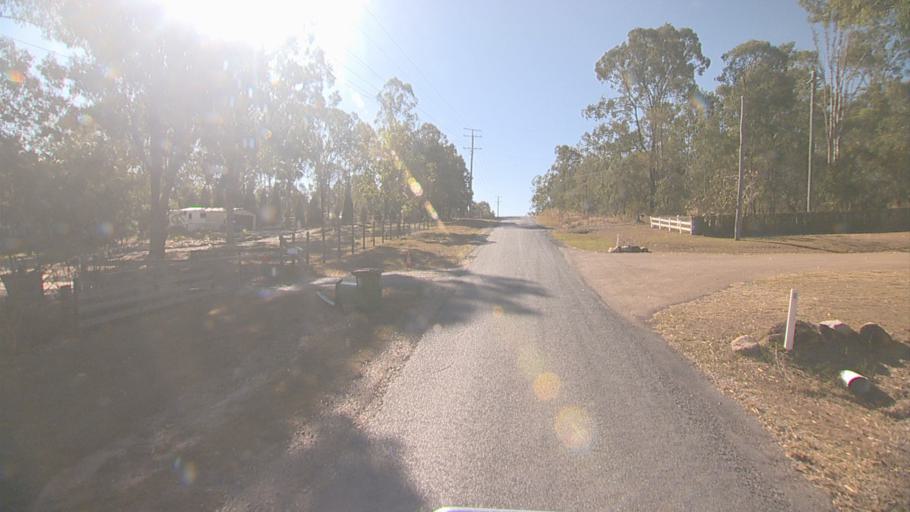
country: AU
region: Queensland
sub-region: Logan
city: Cedar Vale
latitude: -27.8618
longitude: 153.0266
